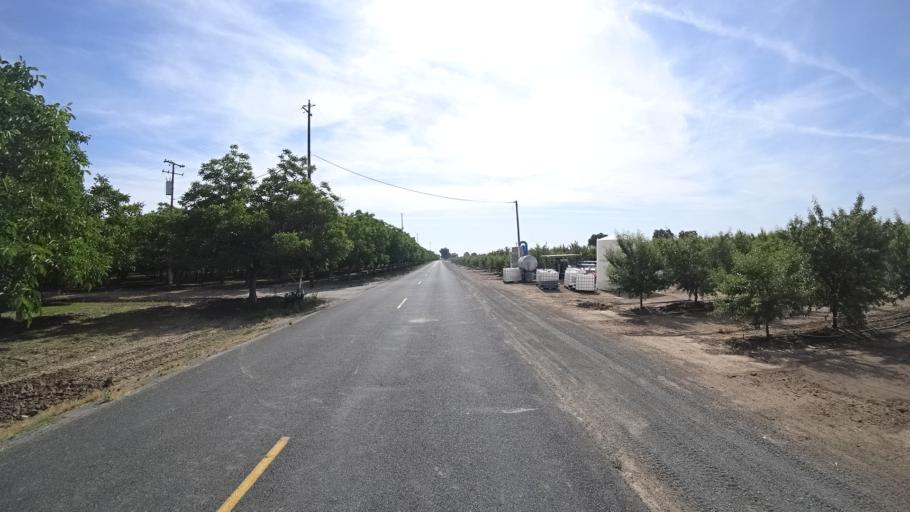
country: US
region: California
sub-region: Fresno County
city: Laton
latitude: 36.4158
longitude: -119.6583
